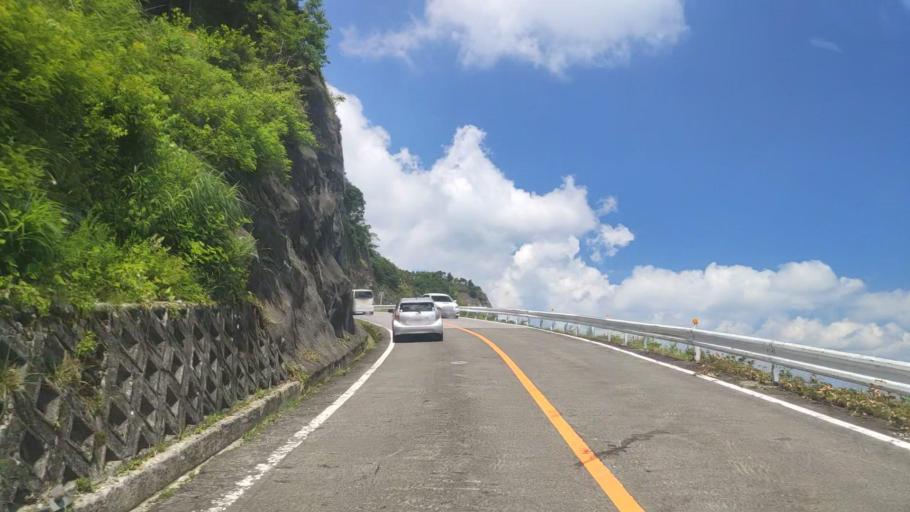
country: JP
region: Gifu
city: Tarui
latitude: 35.4260
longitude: 136.4207
